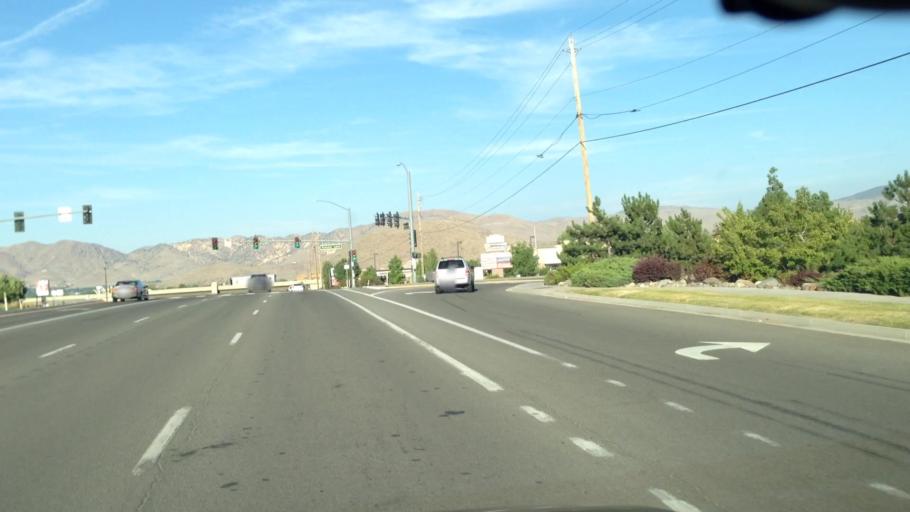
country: US
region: Nevada
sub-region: Washoe County
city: Reno
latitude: 39.4767
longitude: -119.7947
